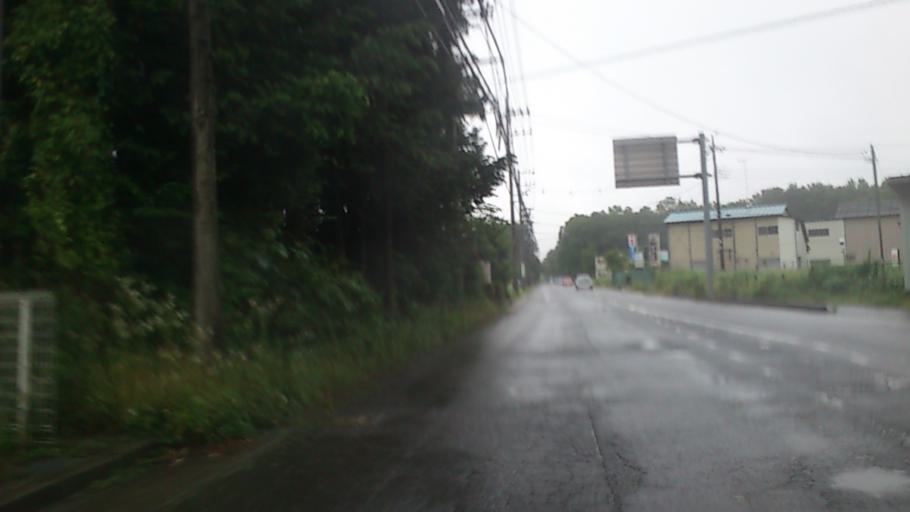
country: JP
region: Tochigi
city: Otawara
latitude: 36.9183
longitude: 139.9738
